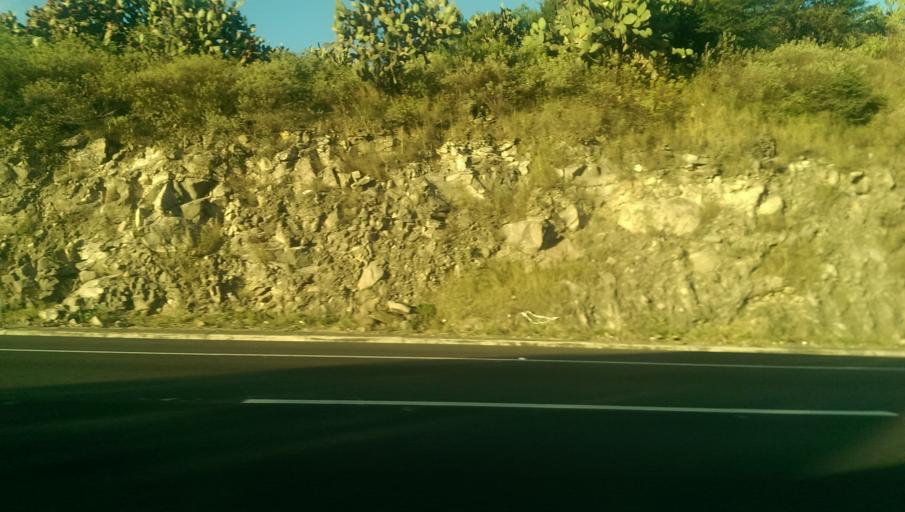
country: MX
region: Hidalgo
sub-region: Huichapan
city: Llano Largo
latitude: 20.2166
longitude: -99.7993
